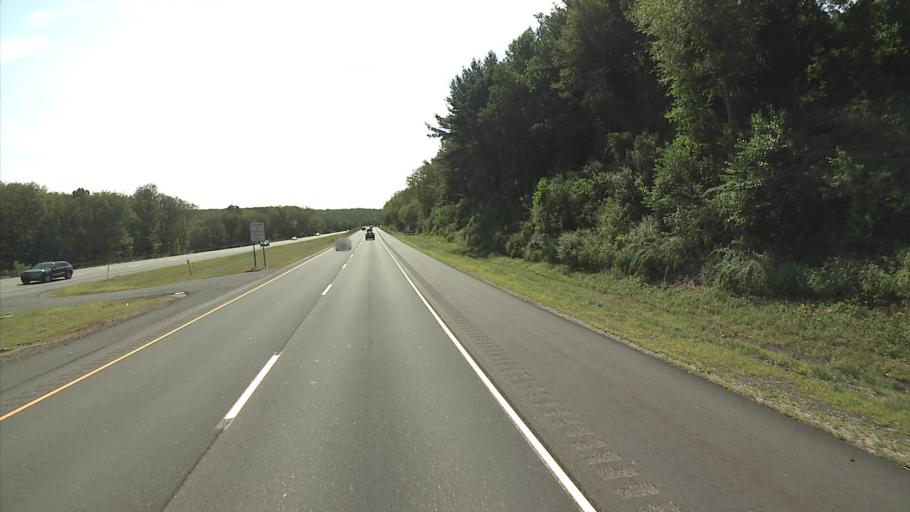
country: US
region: Connecticut
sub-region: Hartford County
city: Terramuggus
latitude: 41.6303
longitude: -72.4515
